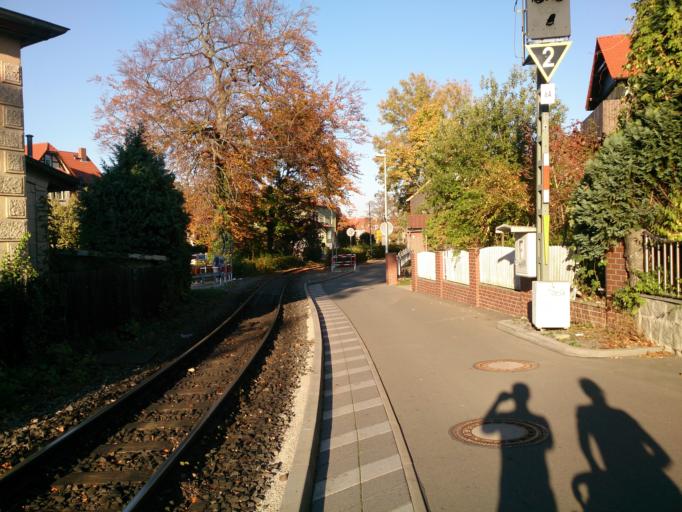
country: DE
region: Saxony-Anhalt
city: Wernigerode
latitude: 51.8313
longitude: 10.7788
